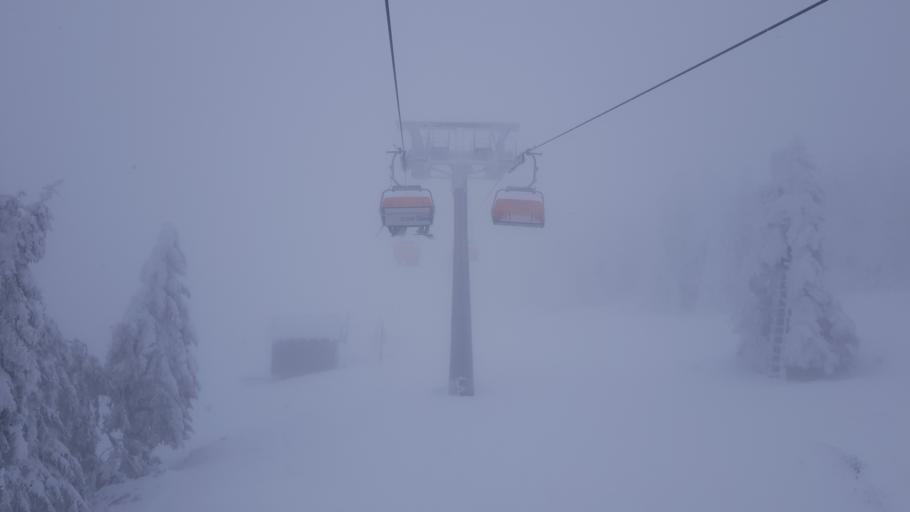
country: DE
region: Saxony
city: Kurort Oberwiesenthal
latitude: 50.3927
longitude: 12.9632
